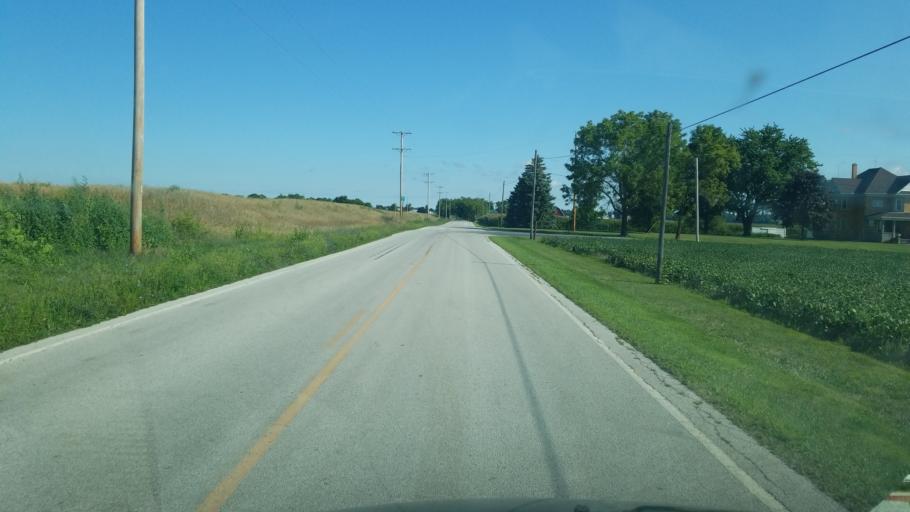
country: US
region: Ohio
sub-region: Wyandot County
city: Carey
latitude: 40.9817
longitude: -83.3676
